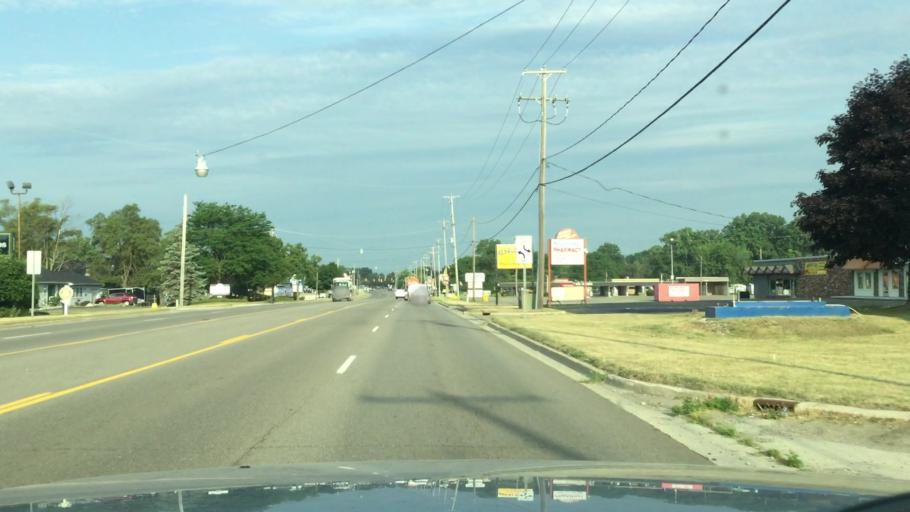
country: US
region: Michigan
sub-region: Genesee County
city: Flushing
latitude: 43.0604
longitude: -83.8066
